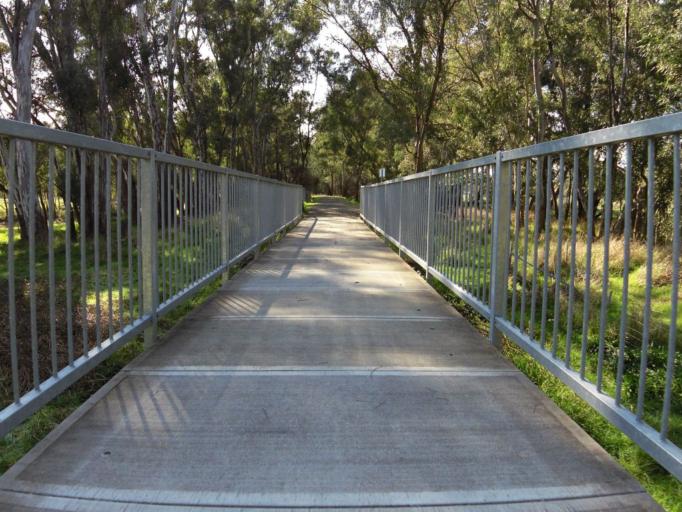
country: AU
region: Victoria
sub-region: Murrindindi
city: Alexandra
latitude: -37.1573
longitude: 145.5711
